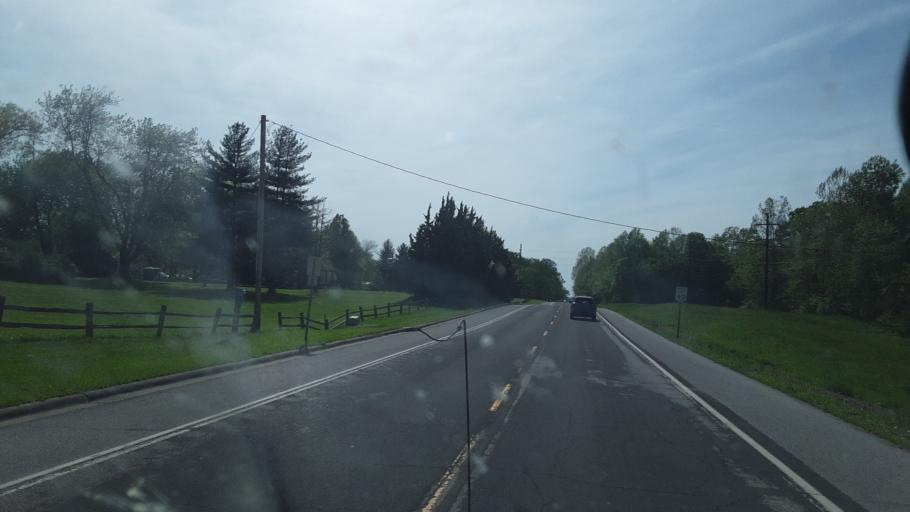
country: US
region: Illinois
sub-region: Jackson County
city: Carbondale
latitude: 37.7007
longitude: -89.2296
